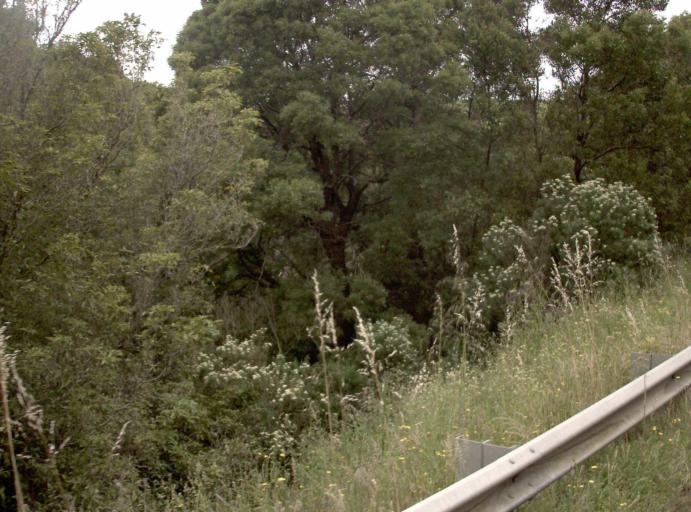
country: AU
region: Victoria
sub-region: Latrobe
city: Moe
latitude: -38.5975
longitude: 146.1273
